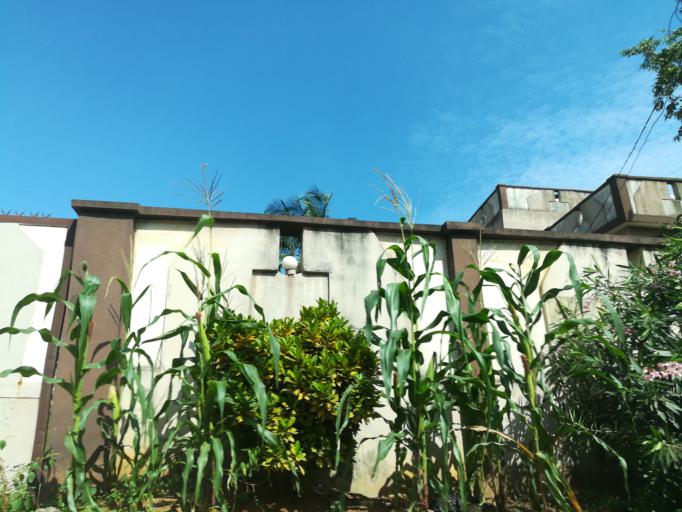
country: NG
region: Lagos
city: Ikorodu
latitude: 6.6021
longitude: 3.5029
